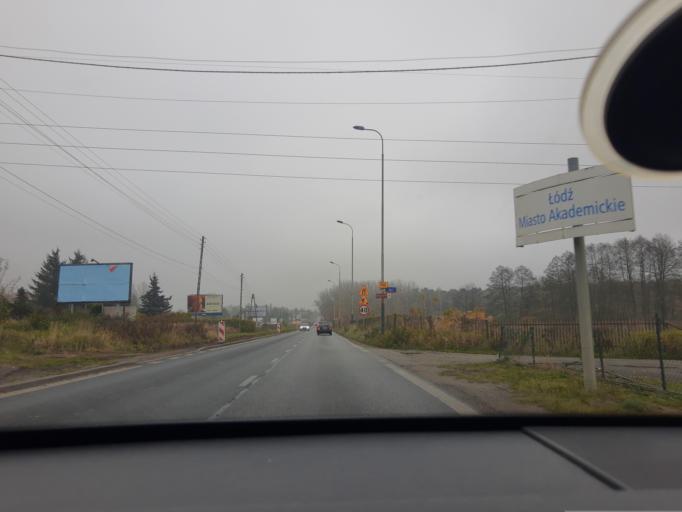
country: PL
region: Lodz Voivodeship
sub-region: Powiat pabianicki
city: Konstantynow Lodzki
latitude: 51.7518
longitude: 19.3732
